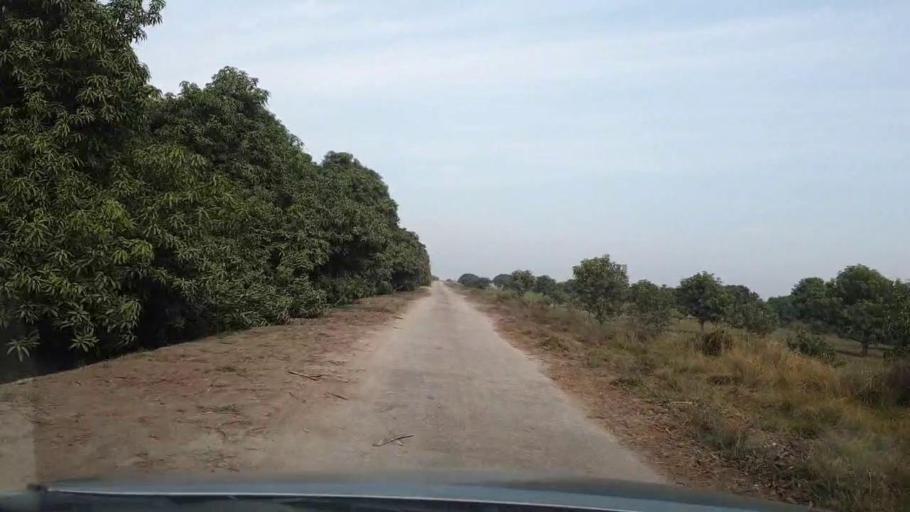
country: PK
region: Sindh
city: Matiari
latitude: 25.5564
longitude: 68.5410
